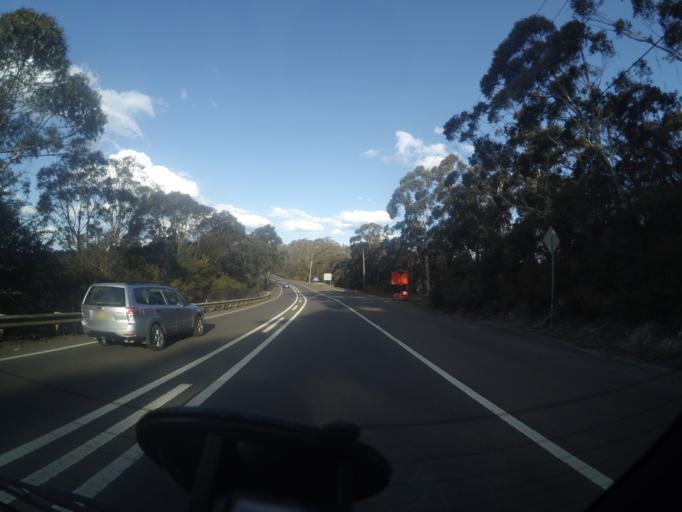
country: AU
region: New South Wales
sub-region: Blue Mountains Municipality
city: Katoomba
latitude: -33.7050
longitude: 150.2928
